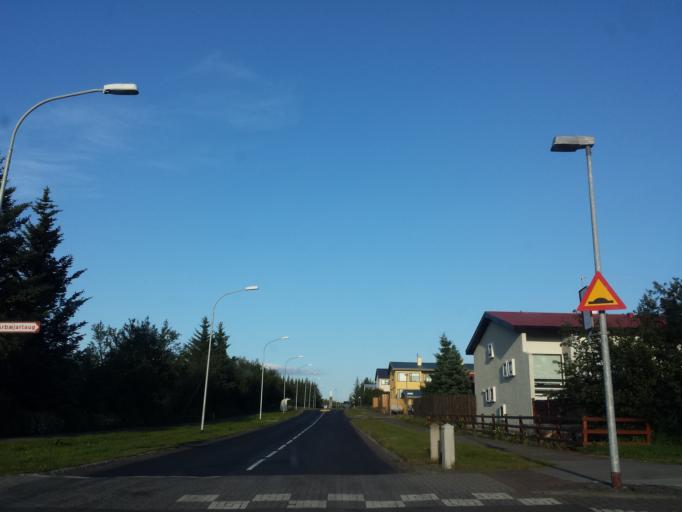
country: IS
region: Capital Region
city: Mosfellsbaer
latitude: 64.1152
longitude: -21.7900
